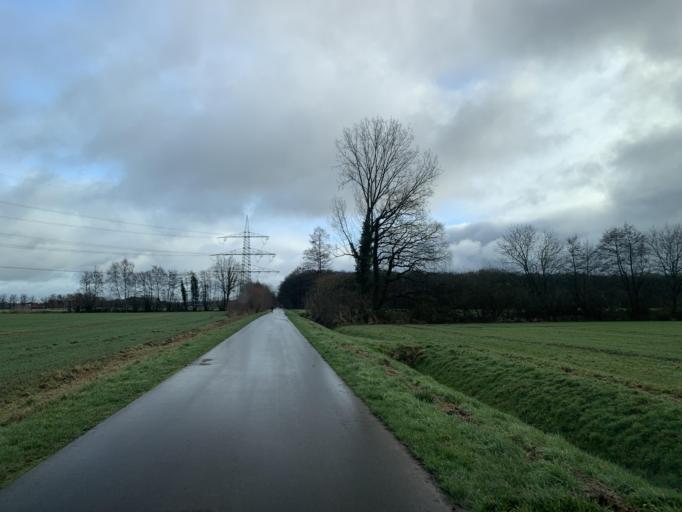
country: DE
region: North Rhine-Westphalia
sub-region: Regierungsbezirk Munster
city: Senden
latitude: 51.9434
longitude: 7.5017
